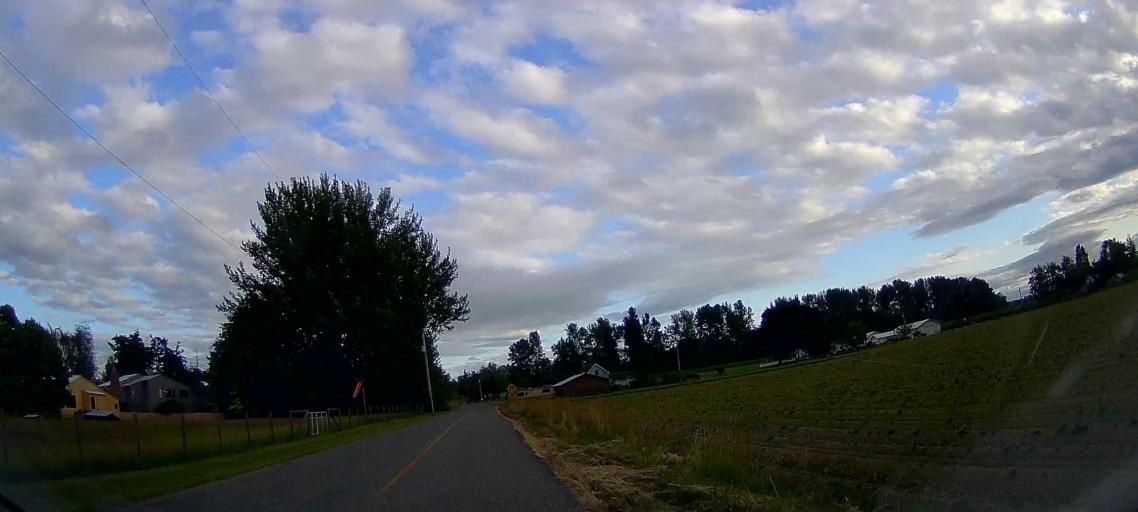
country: US
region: Washington
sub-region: Skagit County
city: Mount Vernon
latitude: 48.3863
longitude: -122.3841
